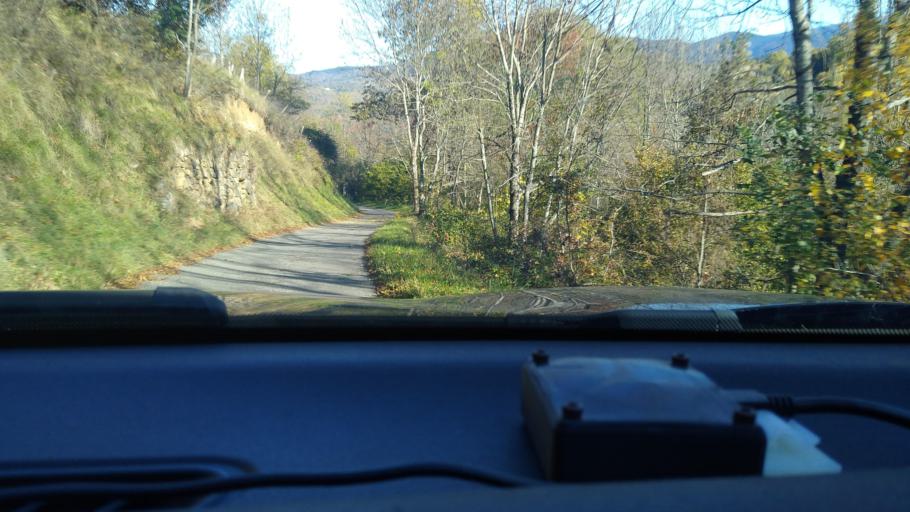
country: FR
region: Languedoc-Roussillon
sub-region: Departement de l'Aude
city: Quillan
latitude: 42.7306
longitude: 2.0634
